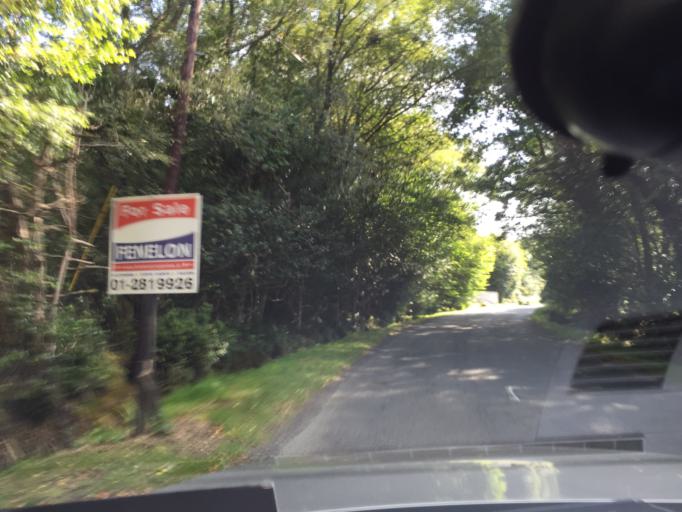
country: IE
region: Leinster
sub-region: Wicklow
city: Rathdrum
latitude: 53.0257
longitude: -6.3078
